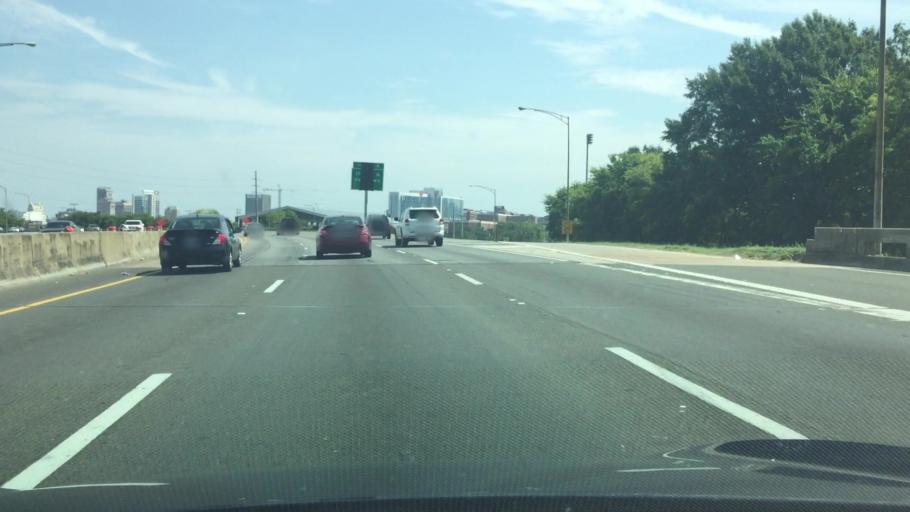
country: US
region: Alabama
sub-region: Jefferson County
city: Birmingham
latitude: 33.4968
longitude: -86.8155
